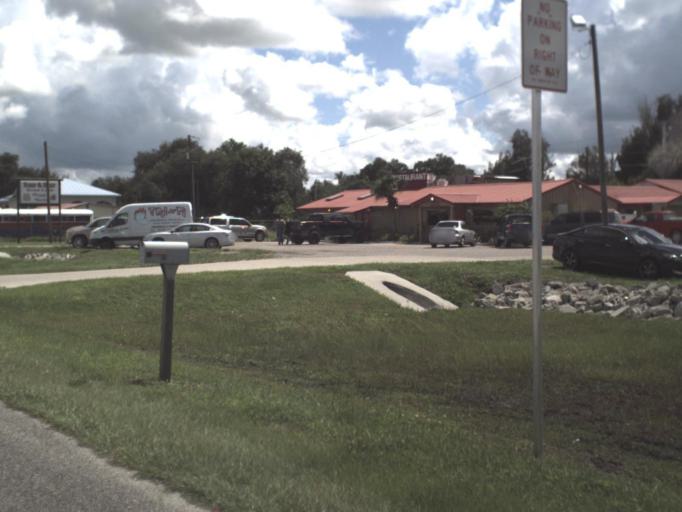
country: US
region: Florida
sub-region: DeSoto County
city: Arcadia
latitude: 27.2090
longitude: -81.8400
